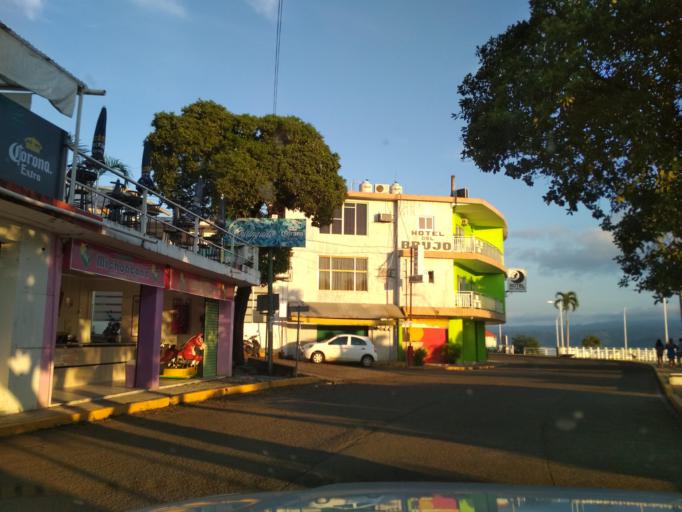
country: MX
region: Veracruz
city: Catemaco
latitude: 18.4171
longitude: -95.1097
